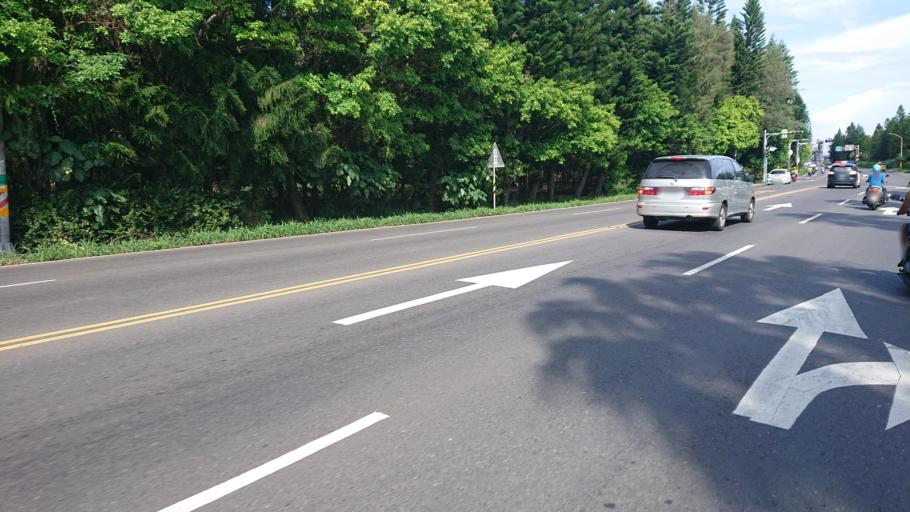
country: TW
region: Taiwan
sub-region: Penghu
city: Ma-kung
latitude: 23.5548
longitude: 119.6072
